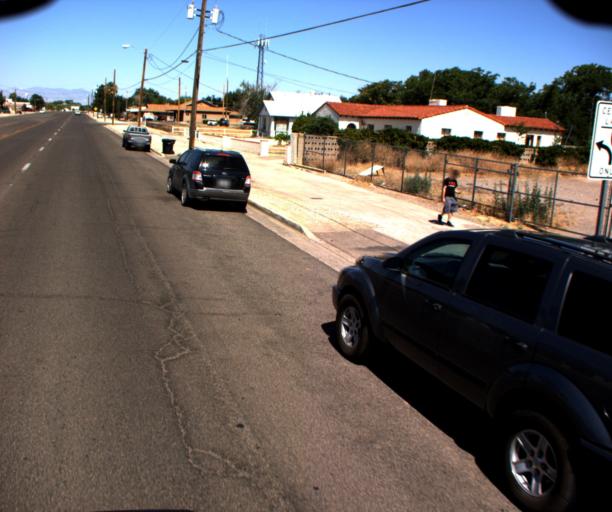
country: US
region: Arizona
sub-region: Graham County
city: Pima
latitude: 32.8963
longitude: -109.8279
